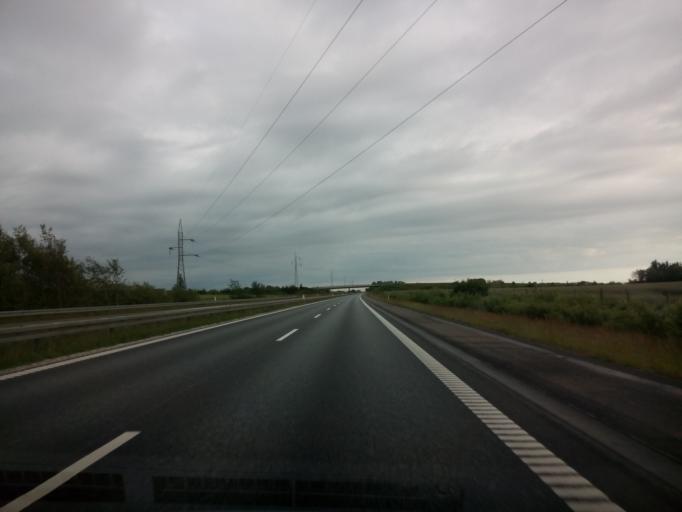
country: DK
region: North Denmark
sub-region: Hjorring Kommune
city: Vra
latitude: 57.3400
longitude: 10.0290
